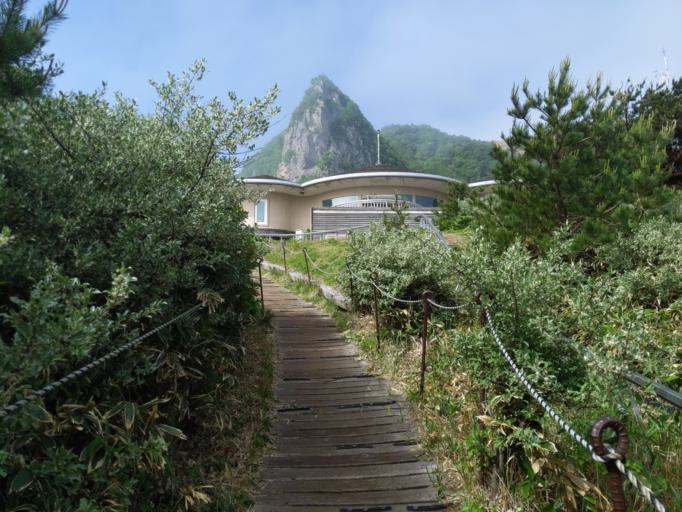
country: KR
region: Jeju-do
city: Seogwipo
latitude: 33.3770
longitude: 126.5308
